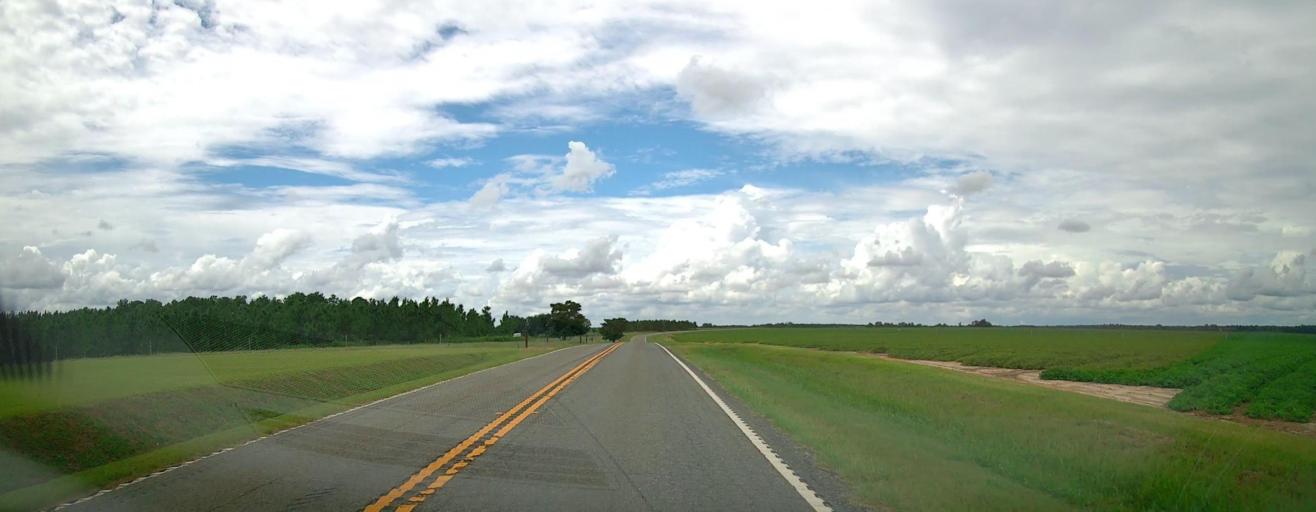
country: US
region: Georgia
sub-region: Dooly County
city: Unadilla
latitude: 32.2606
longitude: -83.8053
